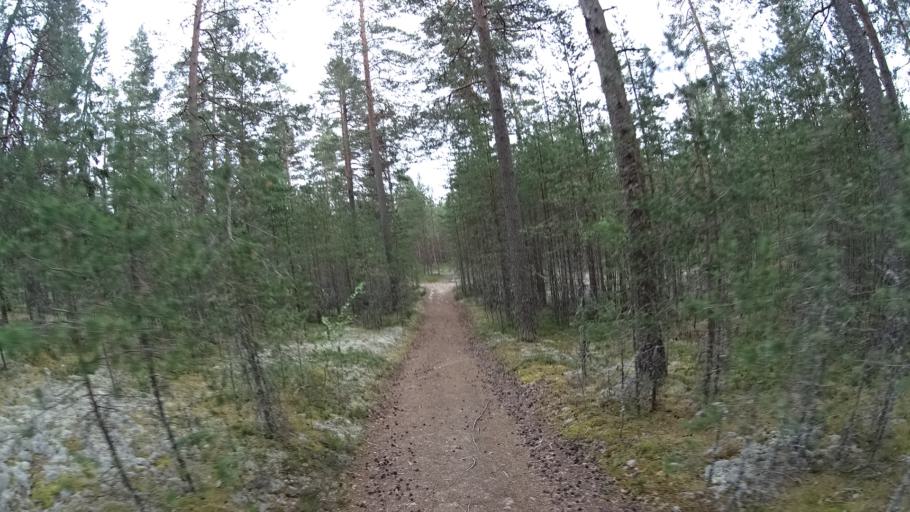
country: FI
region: Satakunta
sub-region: Pohjois-Satakunta
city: Jaemijaervi
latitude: 61.7698
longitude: 22.7435
